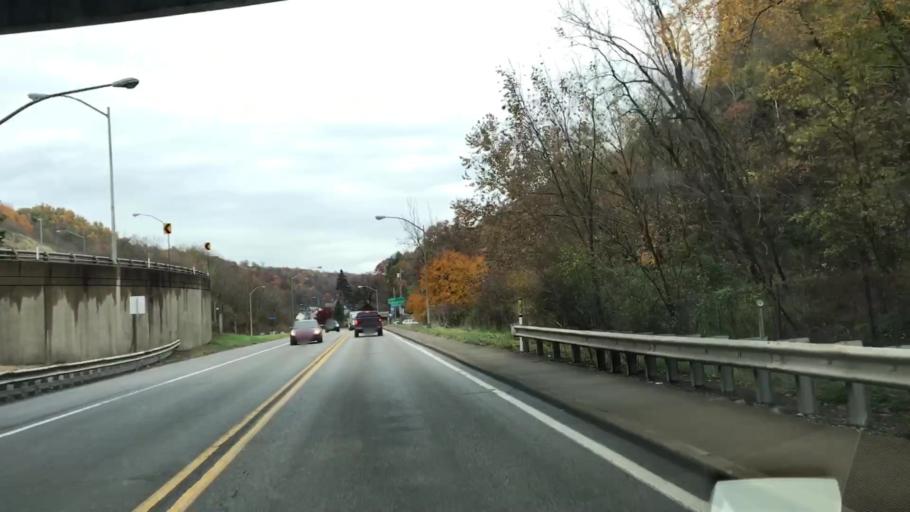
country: US
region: Pennsylvania
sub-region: Allegheny County
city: Coraopolis
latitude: 40.5204
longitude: -80.1305
